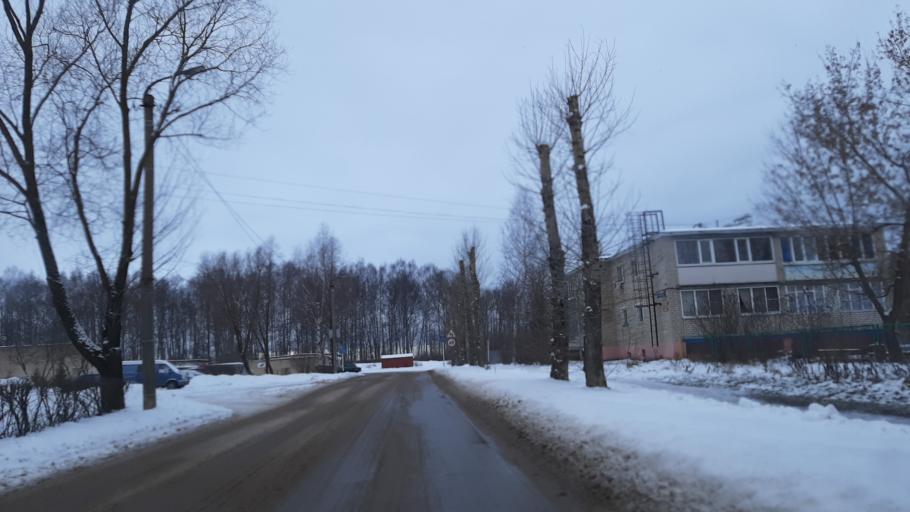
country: RU
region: Kostroma
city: Volgorechensk
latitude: 57.4439
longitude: 41.1462
